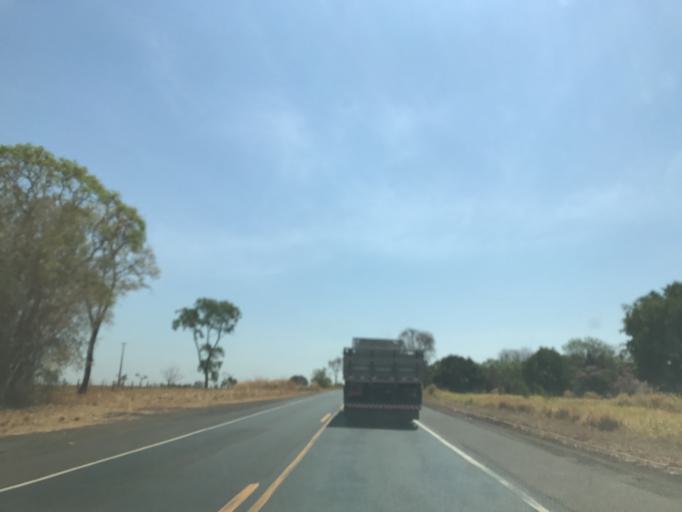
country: BR
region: Minas Gerais
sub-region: Frutal
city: Frutal
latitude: -20.0329
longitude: -49.0490
